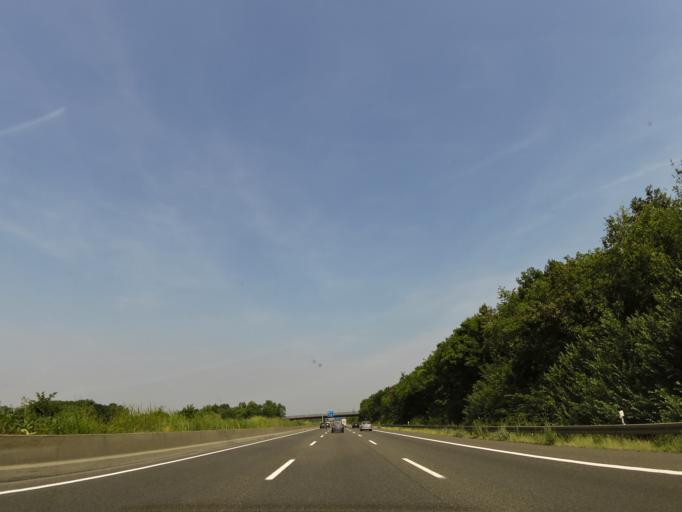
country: DE
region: North Rhine-Westphalia
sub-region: Regierungsbezirk Koln
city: Erftstadt
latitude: 50.7866
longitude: 6.8074
